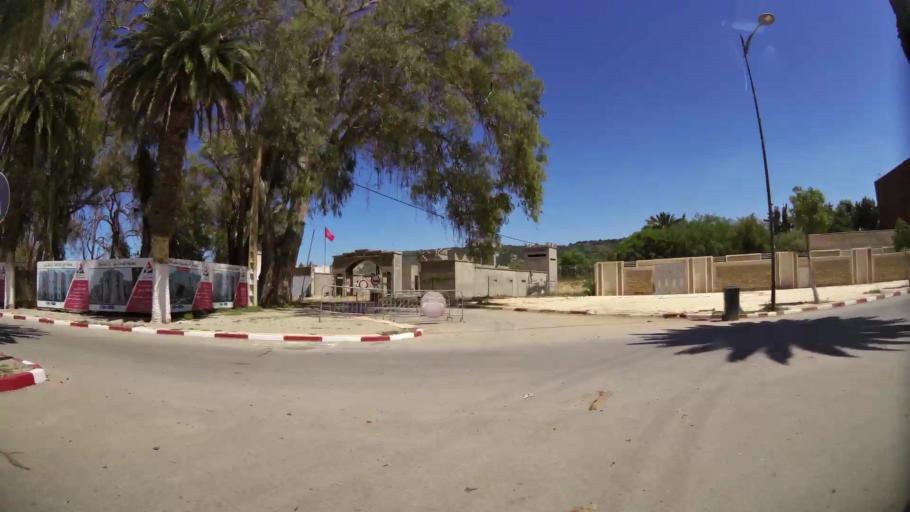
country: MA
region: Oriental
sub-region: Berkane-Taourirt
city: Madagh
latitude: 35.0789
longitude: -2.2137
